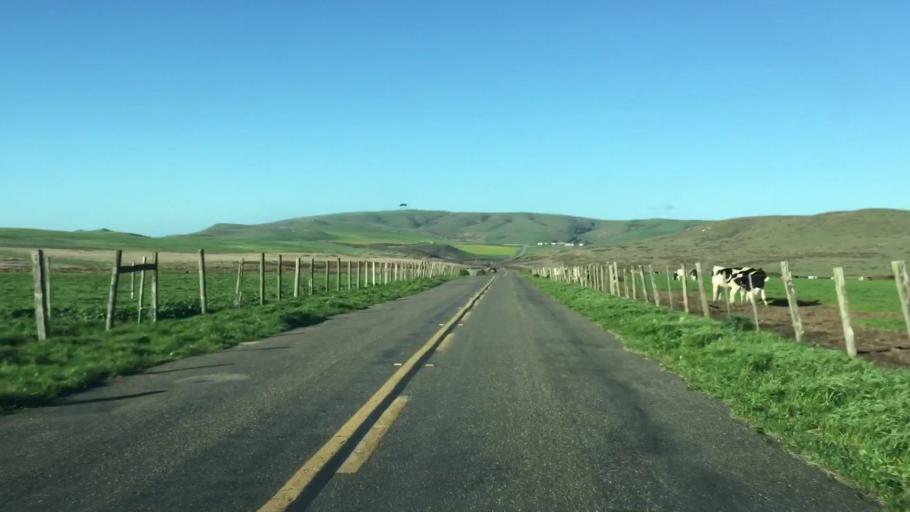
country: US
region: California
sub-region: Marin County
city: Inverness
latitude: 38.1395
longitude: -122.9360
